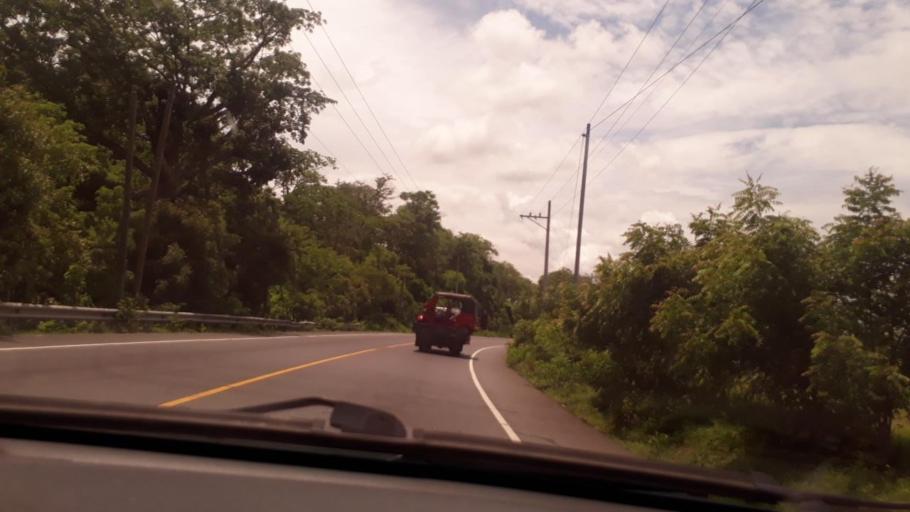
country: GT
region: Zacapa
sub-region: Municipio de Zacapa
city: Gualan
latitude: 15.1345
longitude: -89.3440
